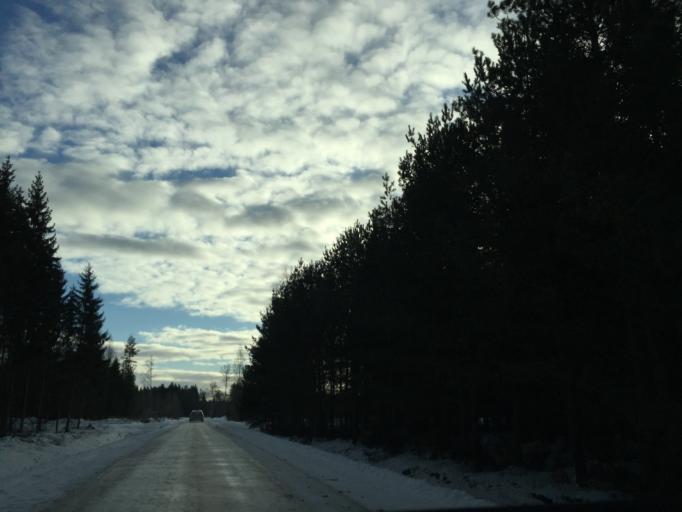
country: LV
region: Ogre
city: Jumprava
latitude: 56.5511
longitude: 24.8582
